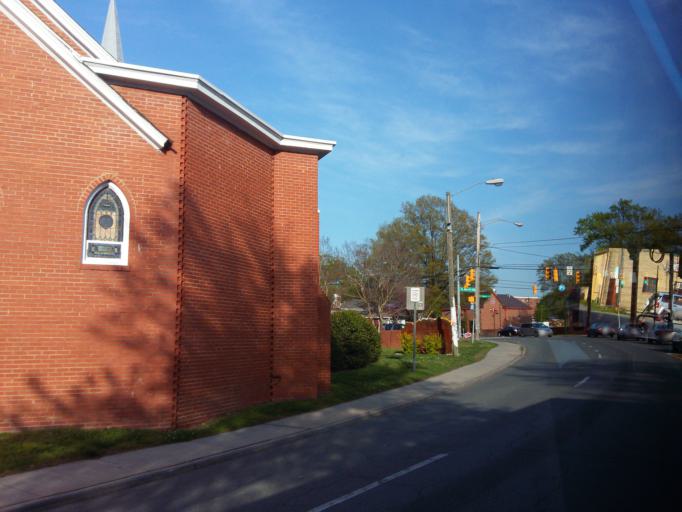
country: US
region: North Carolina
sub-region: Orange County
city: Carrboro
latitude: 35.9100
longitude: -79.0658
